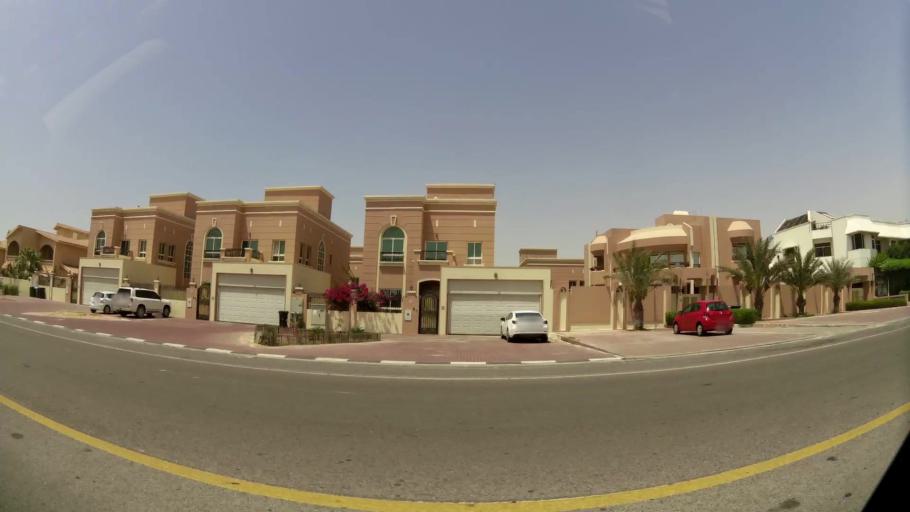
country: AE
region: Dubai
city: Dubai
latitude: 25.1452
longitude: 55.1976
